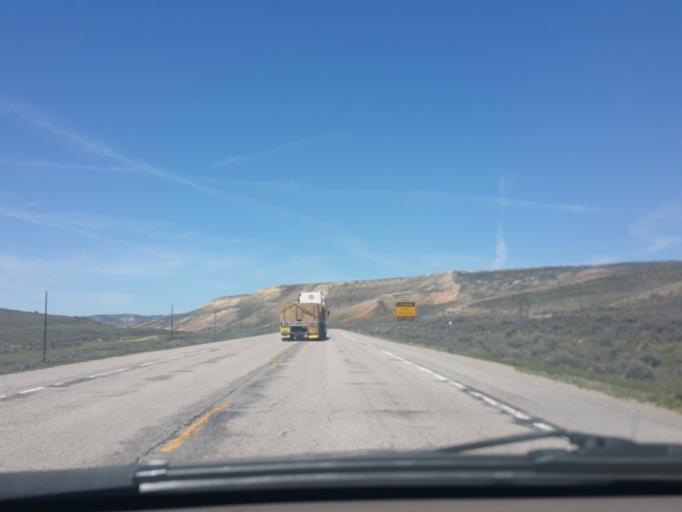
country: US
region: Wyoming
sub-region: Lincoln County
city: Kemmerer
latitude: 41.8111
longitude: -110.6209
